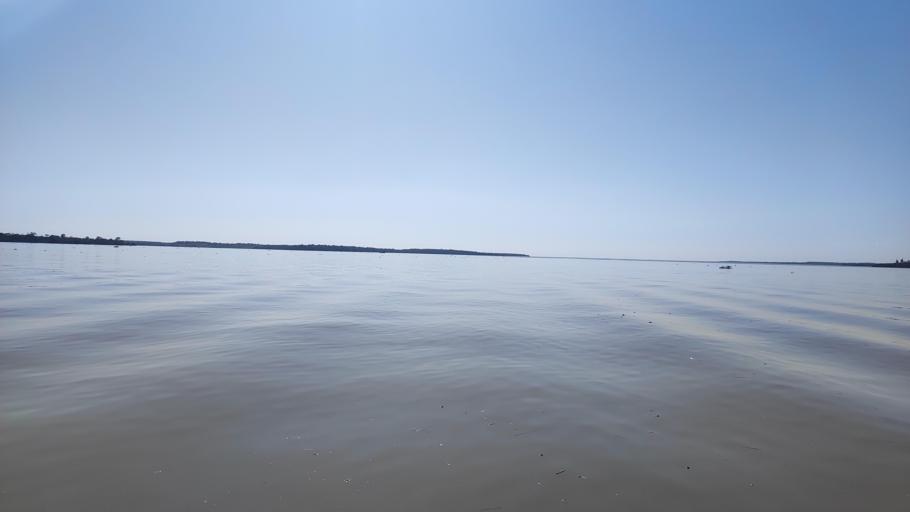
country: PY
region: Itapua
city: San Juan del Parana
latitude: -27.3383
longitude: -55.9943
